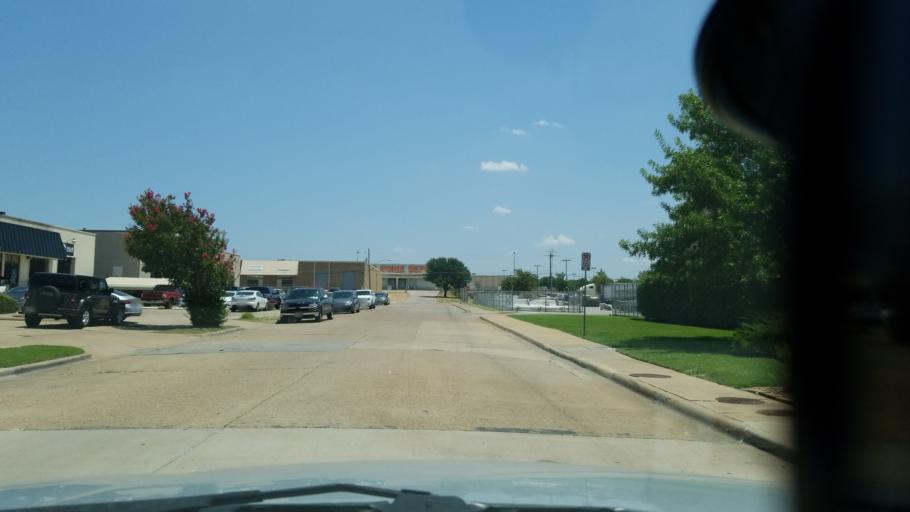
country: US
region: Texas
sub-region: Dallas County
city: Farmers Branch
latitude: 32.9072
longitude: -96.8881
